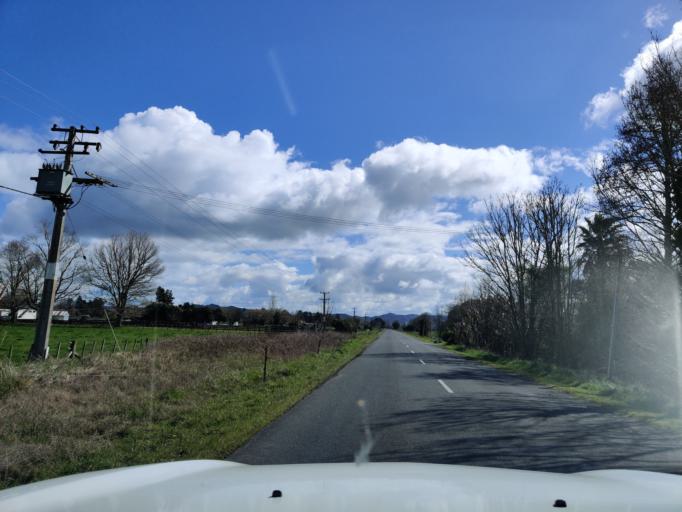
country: NZ
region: Waikato
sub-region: Waikato District
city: Ngaruawahia
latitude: -37.5847
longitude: 175.2830
